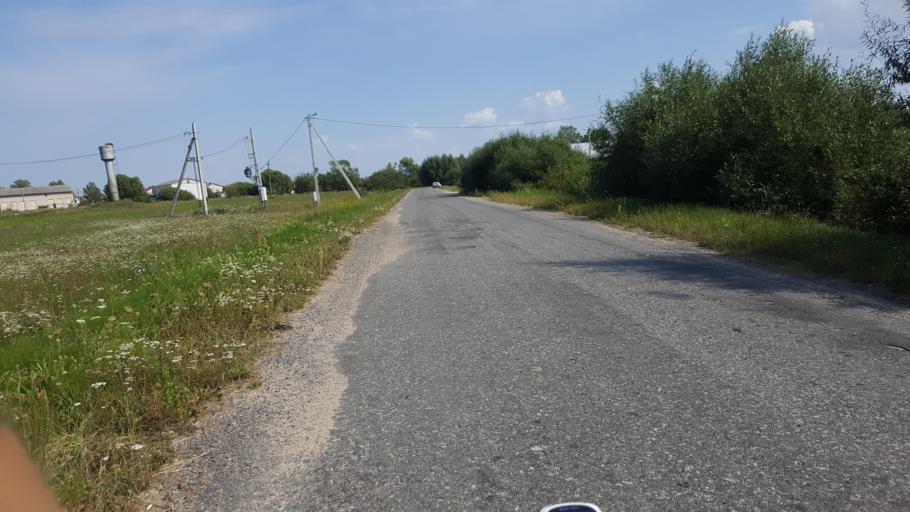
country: PL
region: Podlasie
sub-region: Powiat hajnowski
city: Czeremcha
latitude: 52.4956
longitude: 23.5657
